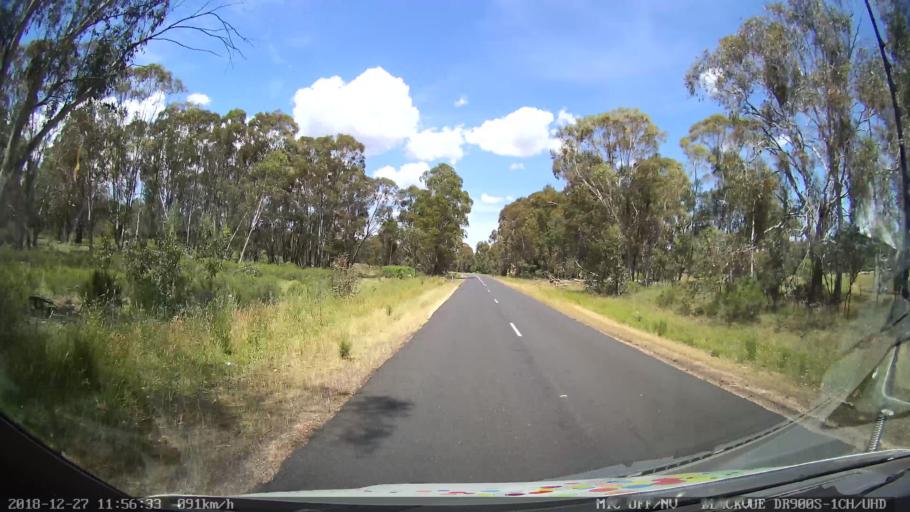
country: AU
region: New South Wales
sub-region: Blayney
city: Blayney
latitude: -33.6998
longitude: 149.3905
